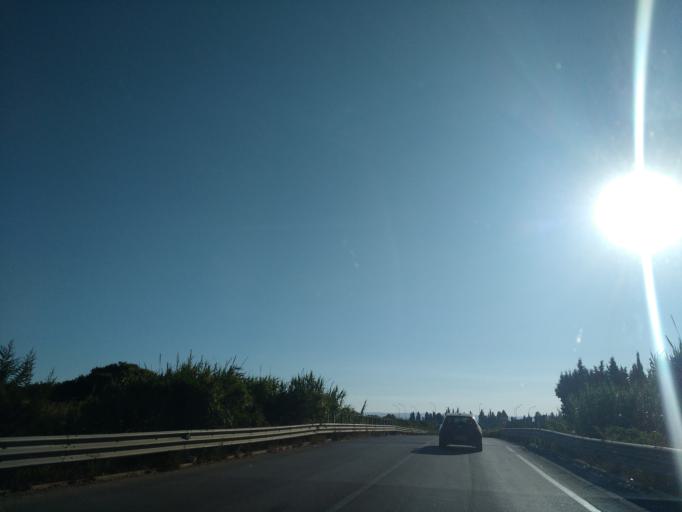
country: IT
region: Sicily
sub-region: Provincia di Siracusa
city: Siracusa
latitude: 37.0652
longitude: 15.2488
